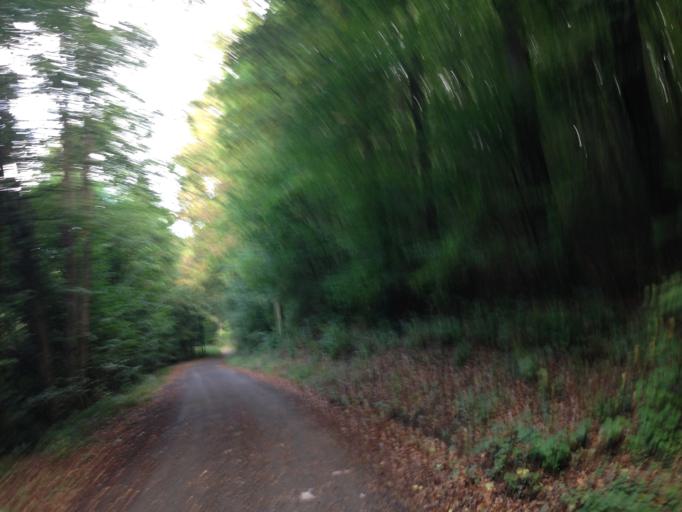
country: DE
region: Hesse
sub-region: Regierungsbezirk Giessen
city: Heuchelheim
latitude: 50.6416
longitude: 8.5644
